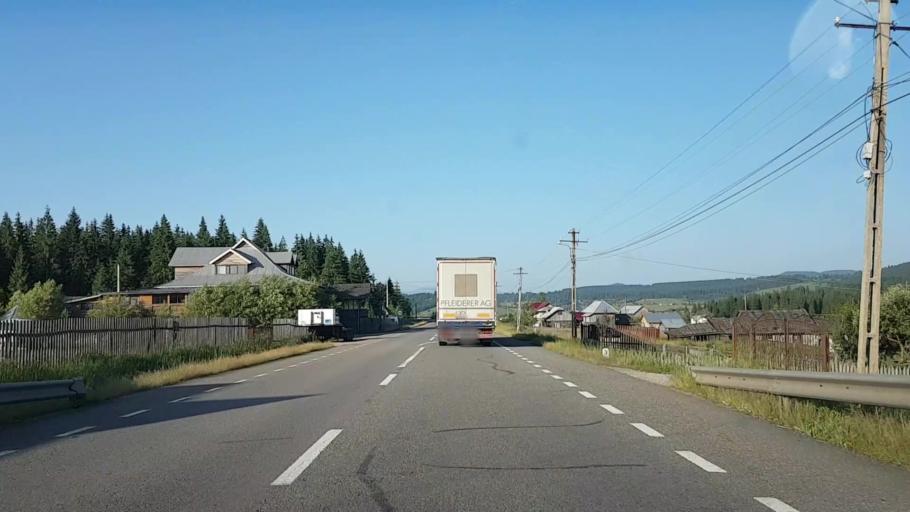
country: RO
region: Suceava
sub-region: Comuna Poiana Stampei
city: Poiana Stampei
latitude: 47.3052
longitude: 25.1183
